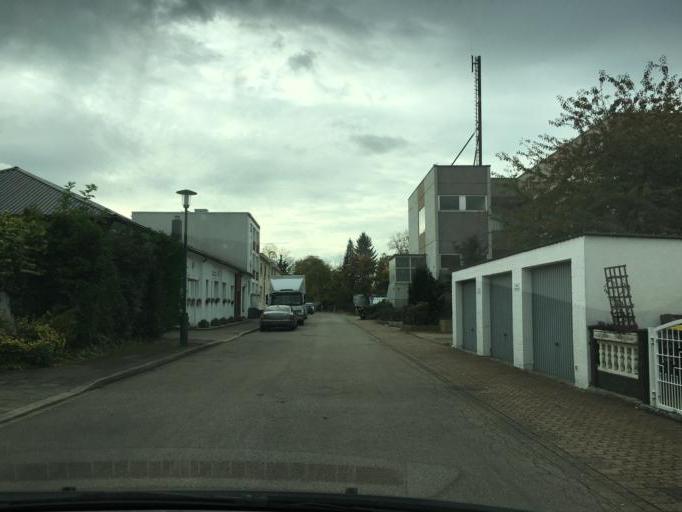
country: DE
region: North Rhine-Westphalia
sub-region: Regierungsbezirk Koln
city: Dueren
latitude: 50.7987
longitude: 6.4672
